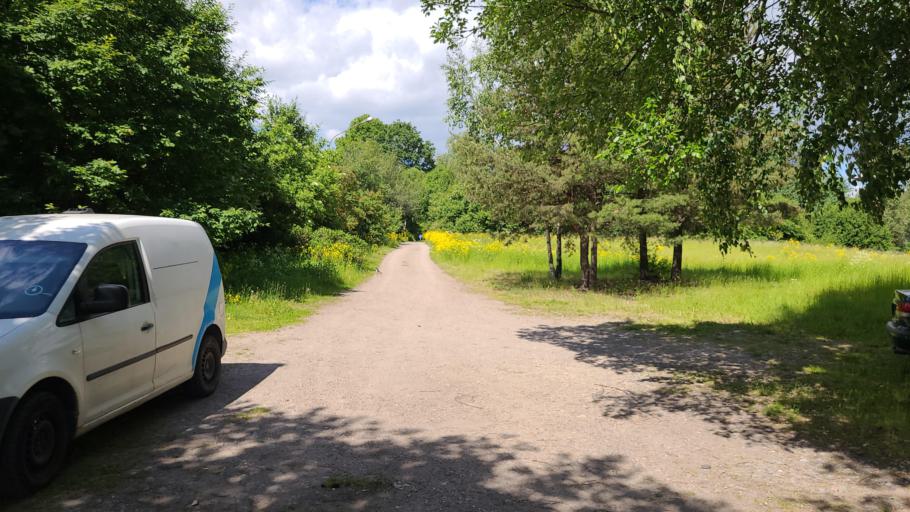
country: SE
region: Stockholm
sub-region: Norrtalje Kommun
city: Bergshamra
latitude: 59.3780
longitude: 18.0183
